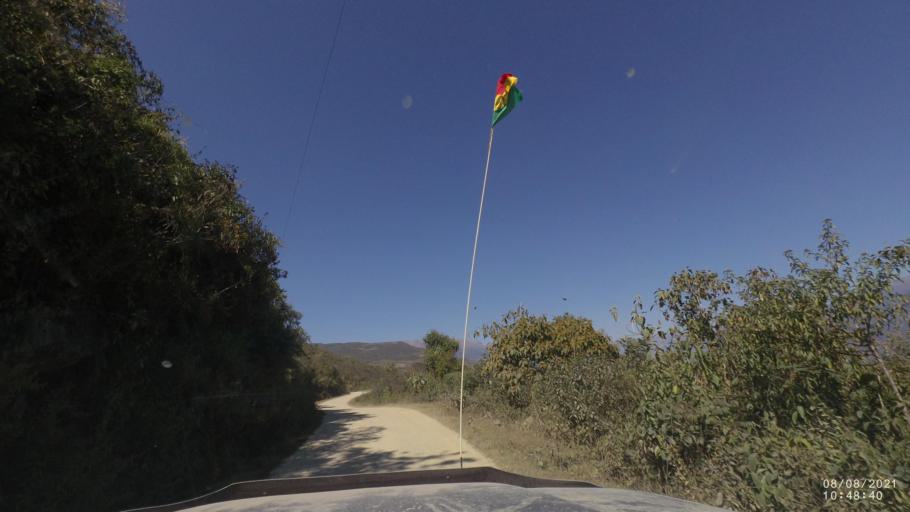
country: BO
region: La Paz
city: Quime
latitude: -16.7161
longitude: -66.7058
